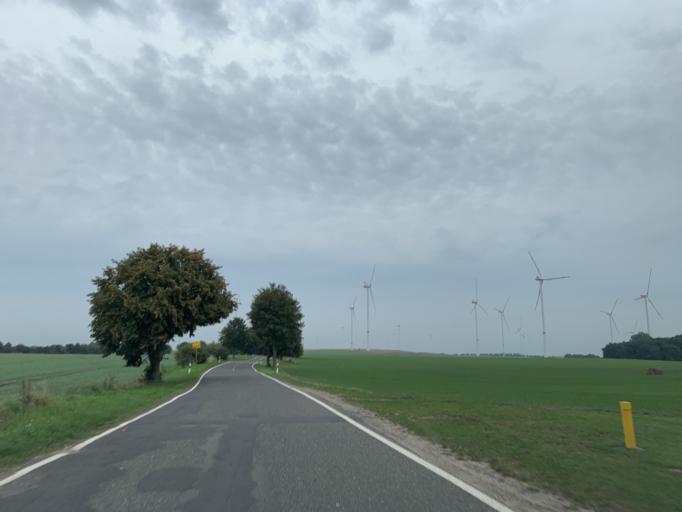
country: DE
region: Brandenburg
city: Mittenwalde
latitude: 53.3122
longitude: 13.6861
